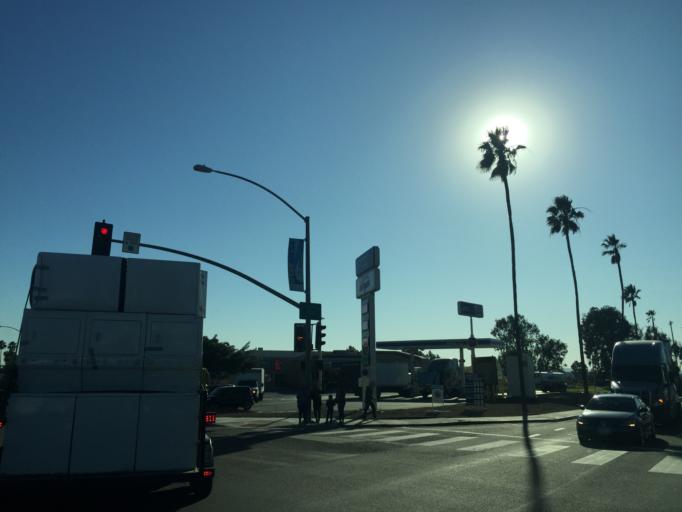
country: MX
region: Baja California
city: Tijuana
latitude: 32.5539
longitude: -116.9424
